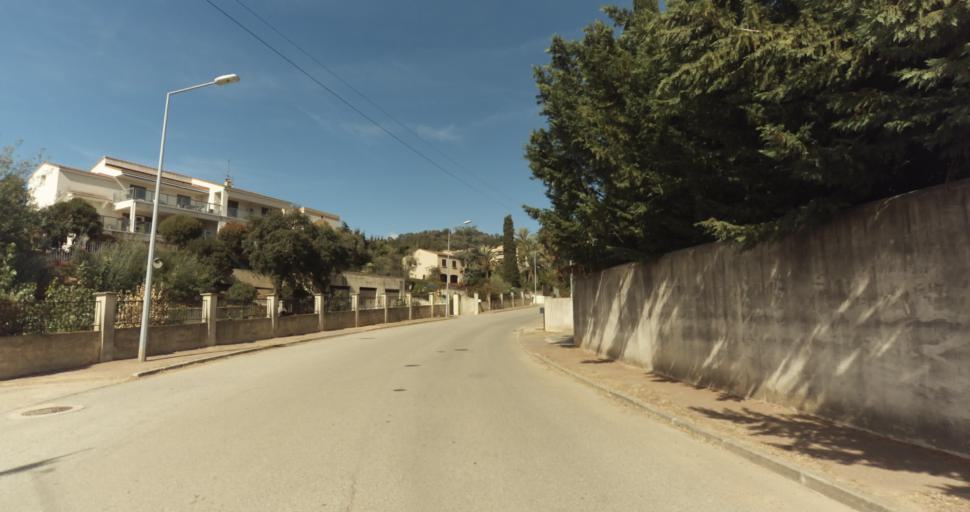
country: FR
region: Corsica
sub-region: Departement de la Corse-du-Sud
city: Ajaccio
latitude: 41.9397
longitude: 8.7639
